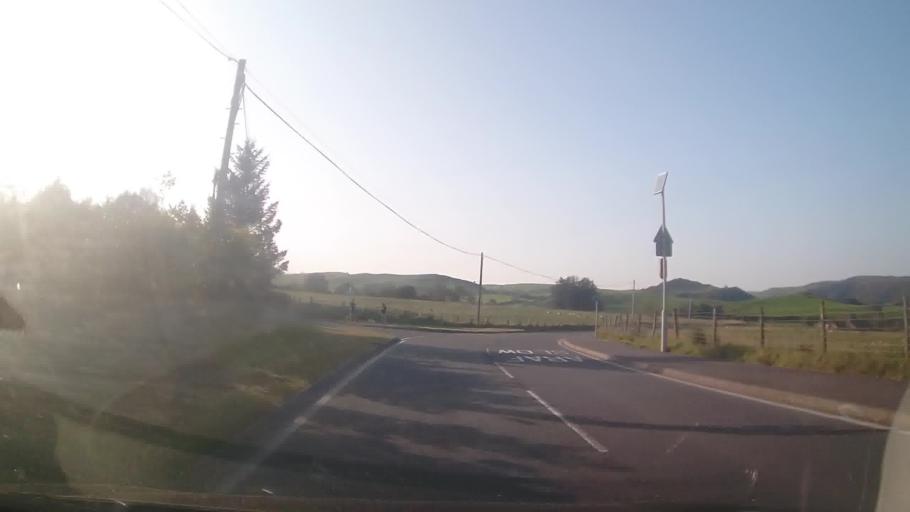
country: GB
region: Wales
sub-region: County of Ceredigion
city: Lledrod
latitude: 52.3711
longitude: -3.8581
